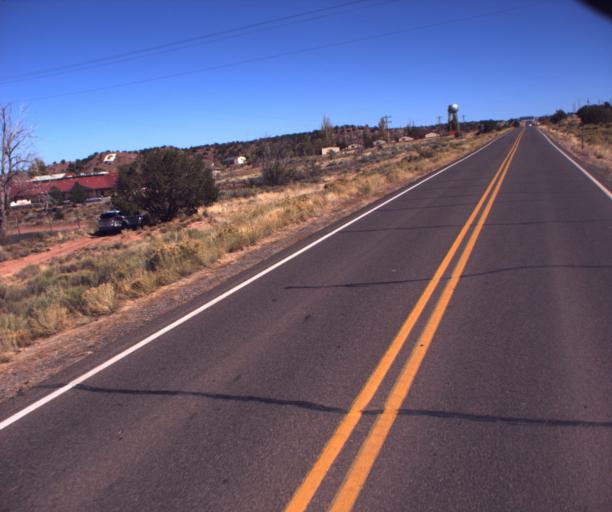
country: US
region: Arizona
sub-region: Apache County
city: Ganado
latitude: 35.7093
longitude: -109.5364
